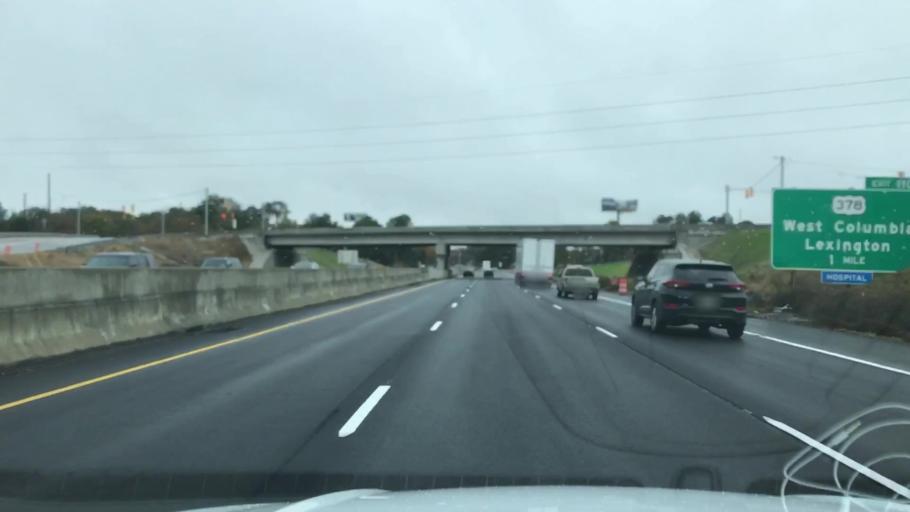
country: US
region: South Carolina
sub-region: Lexington County
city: Springdale
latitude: 33.9876
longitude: -81.1071
